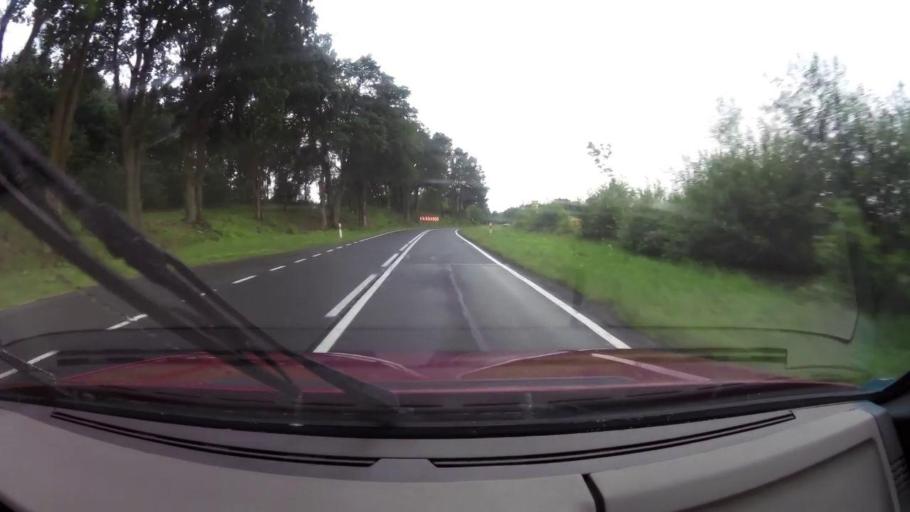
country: PL
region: West Pomeranian Voivodeship
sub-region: Powiat stargardzki
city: Chociwel
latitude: 53.4733
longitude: 15.3641
